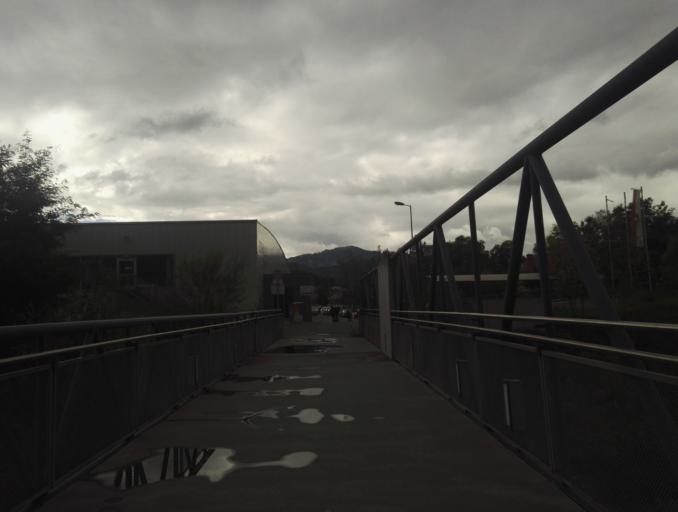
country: AT
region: Styria
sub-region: Politischer Bezirk Leoben
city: Leoben
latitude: 47.3884
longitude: 15.0955
